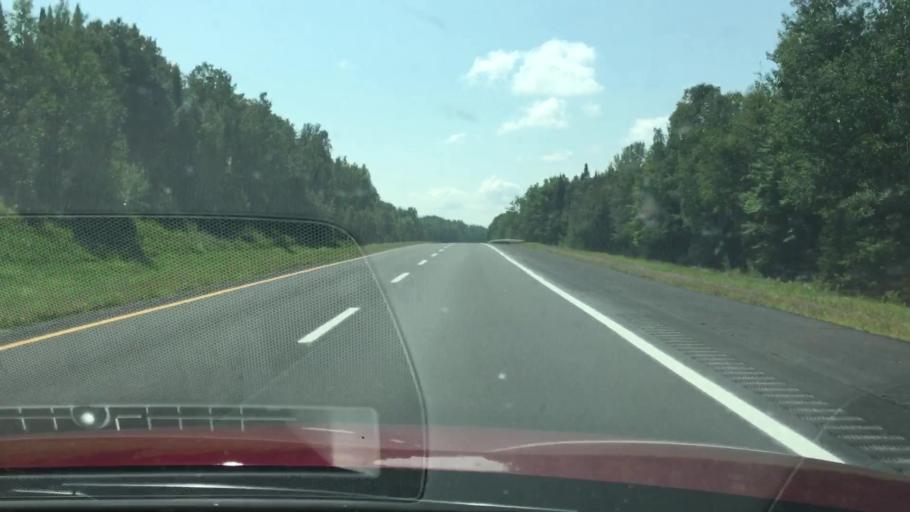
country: US
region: Maine
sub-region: Penobscot County
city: Patten
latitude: 45.9119
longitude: -68.3786
